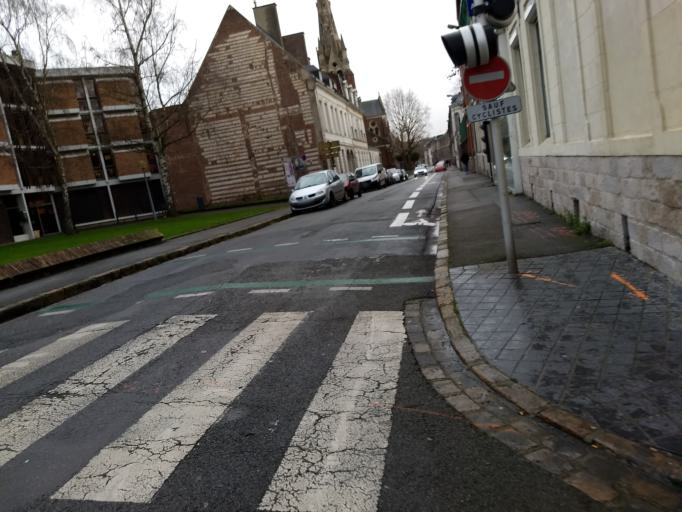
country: FR
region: Nord-Pas-de-Calais
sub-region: Departement du Pas-de-Calais
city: Arras
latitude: 50.2903
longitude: 2.7689
